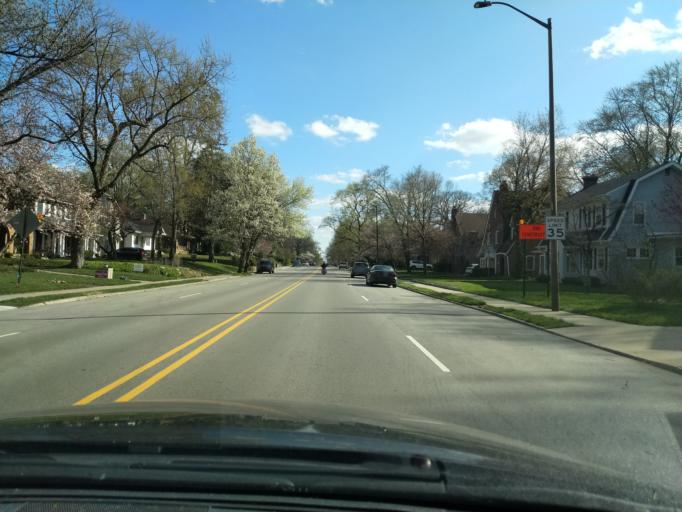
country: US
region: Indiana
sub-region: Marion County
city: Broad Ripple
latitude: 39.8503
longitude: -86.1501
